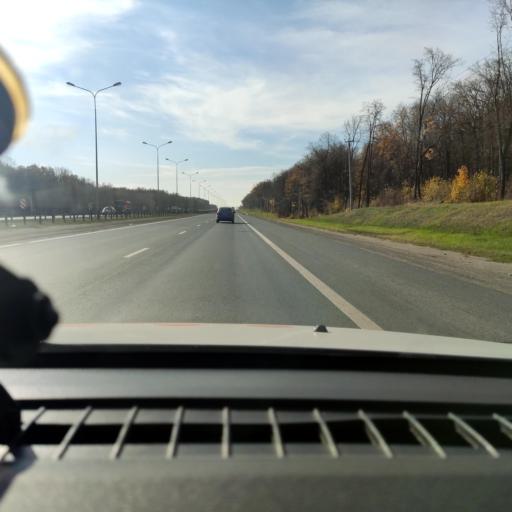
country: RU
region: Samara
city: Novosemeykino
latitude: 53.3456
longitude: 50.3038
